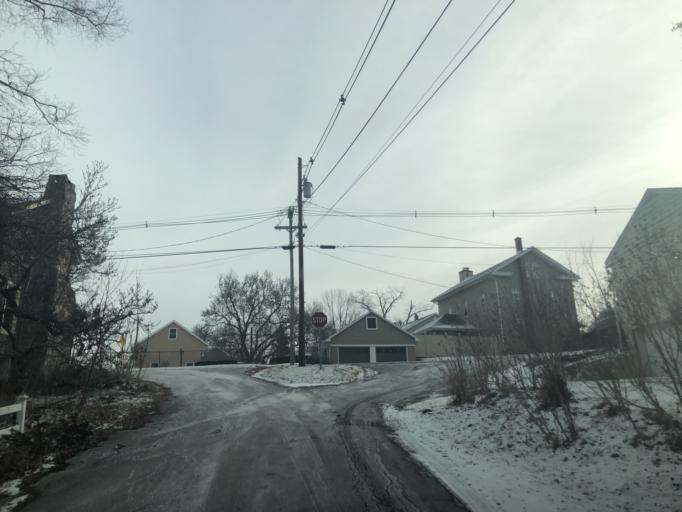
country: US
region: New Jersey
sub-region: Warren County
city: Belvidere
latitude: 40.9306
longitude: -75.0281
